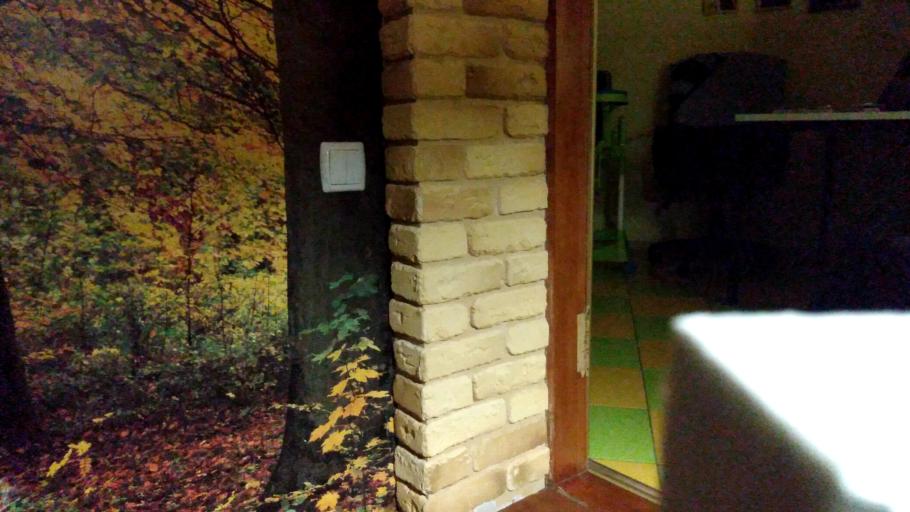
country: RU
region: Vologda
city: Lipin Bor
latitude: 61.0740
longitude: 37.9342
